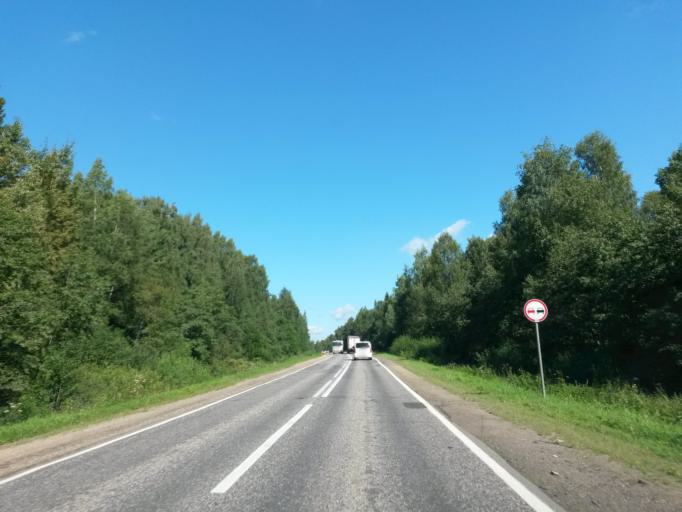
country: RU
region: Jaroslavl
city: Krasnyye Tkachi
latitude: 57.4699
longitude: 39.9086
